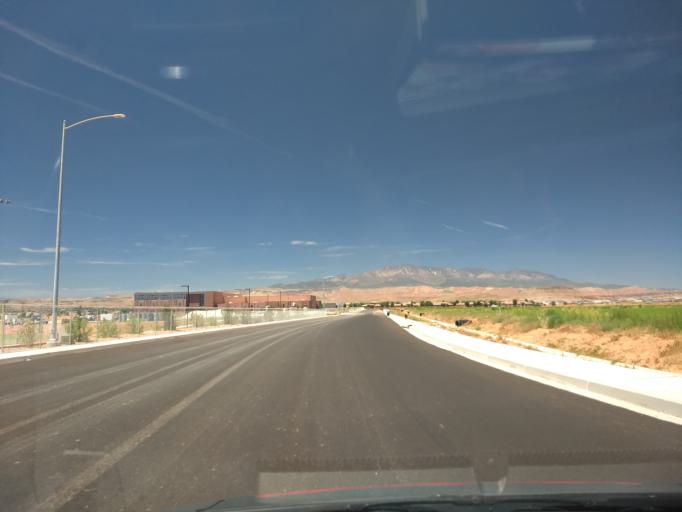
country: US
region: Utah
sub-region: Washington County
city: Washington
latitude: 37.0697
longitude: -113.5062
